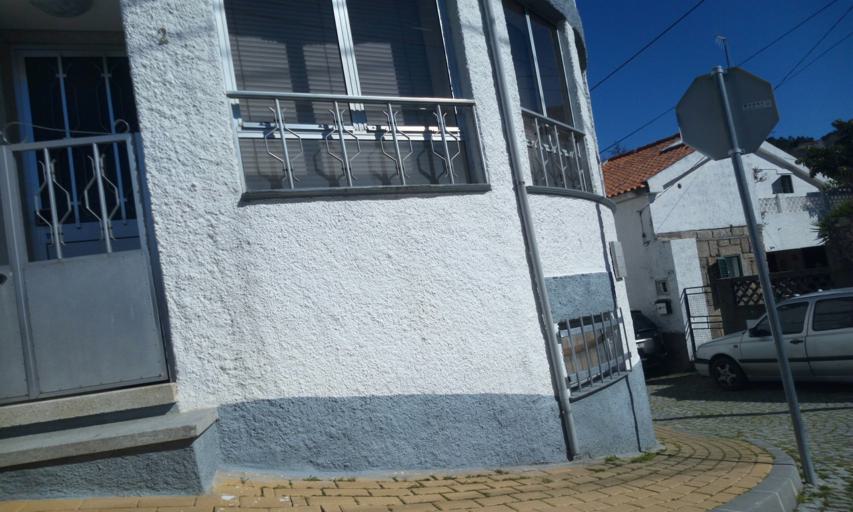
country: PT
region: Guarda
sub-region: Manteigas
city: Manteigas
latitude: 40.4911
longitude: -7.5920
